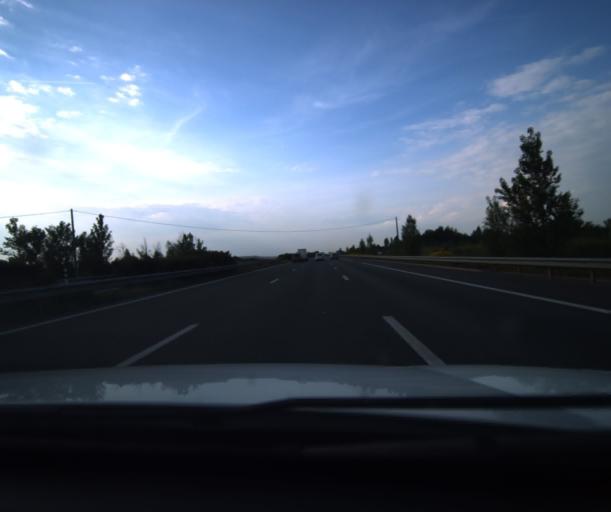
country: FR
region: Midi-Pyrenees
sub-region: Departement du Tarn-et-Garonne
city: Campsas
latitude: 43.8730
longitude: 1.3178
